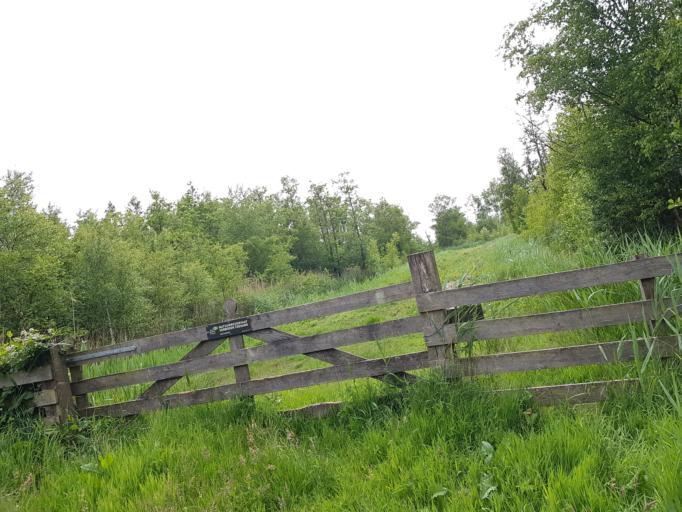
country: NL
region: Friesland
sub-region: Gemeente Tytsjerksteradiel
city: Garyp
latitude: 53.1380
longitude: 5.9460
